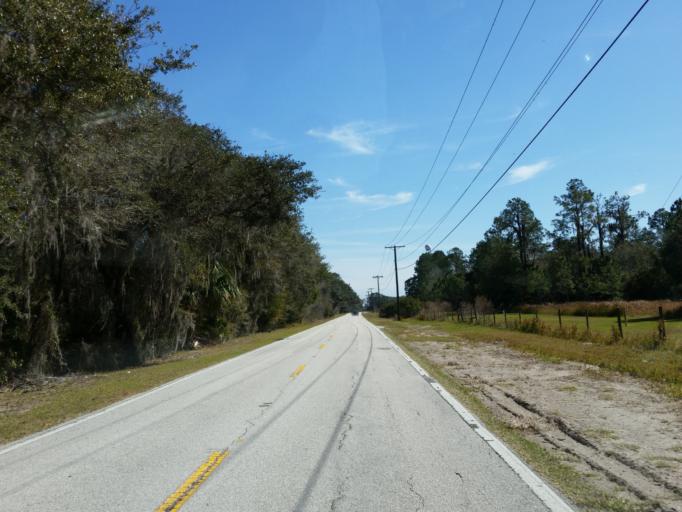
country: US
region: Florida
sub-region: Hillsborough County
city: Boyette
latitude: 27.8213
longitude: -82.2398
